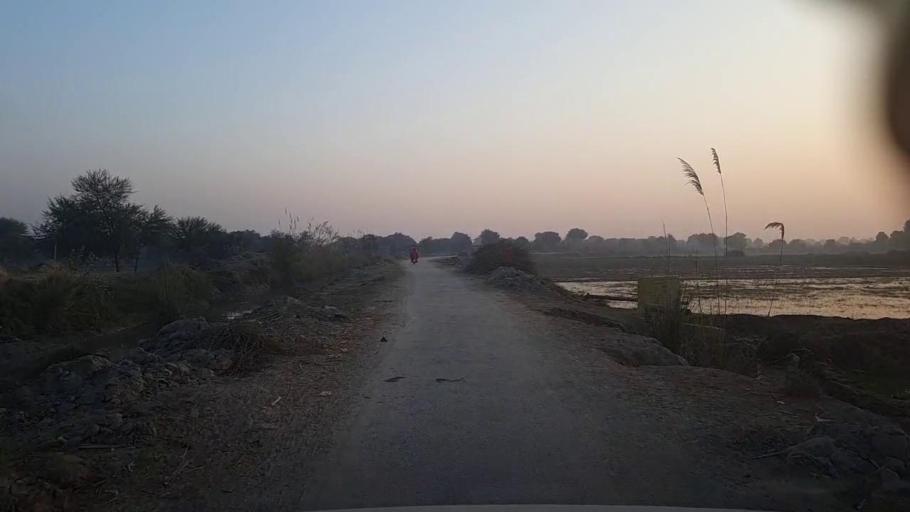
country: PK
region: Sindh
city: Karaundi
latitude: 26.8374
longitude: 68.3693
